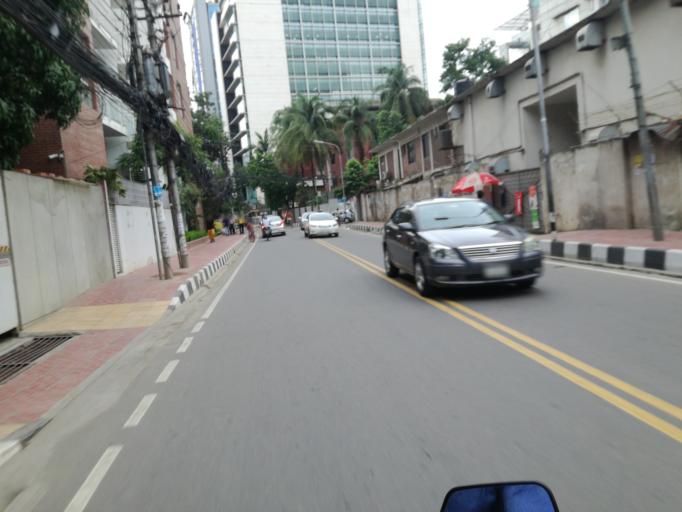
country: BD
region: Dhaka
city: Paltan
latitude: 23.7857
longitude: 90.4162
